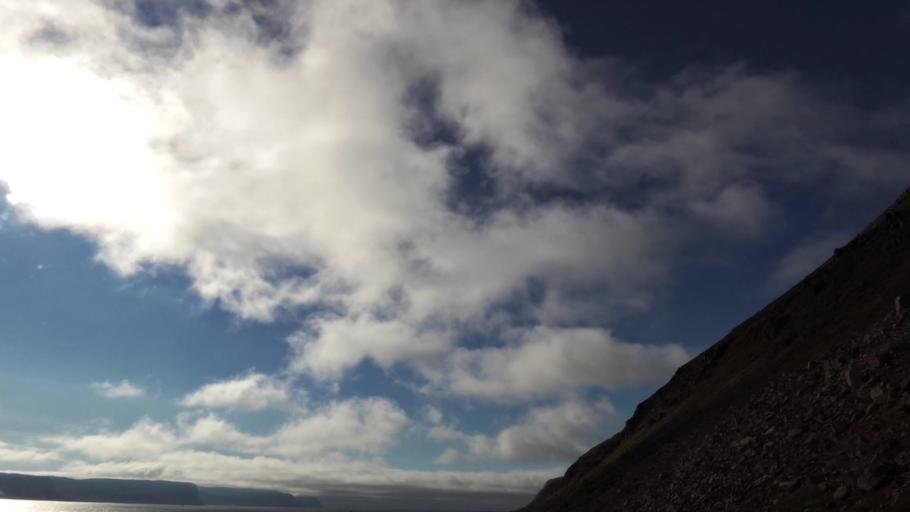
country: IS
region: West
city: Olafsvik
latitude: 65.5632
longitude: -23.9151
